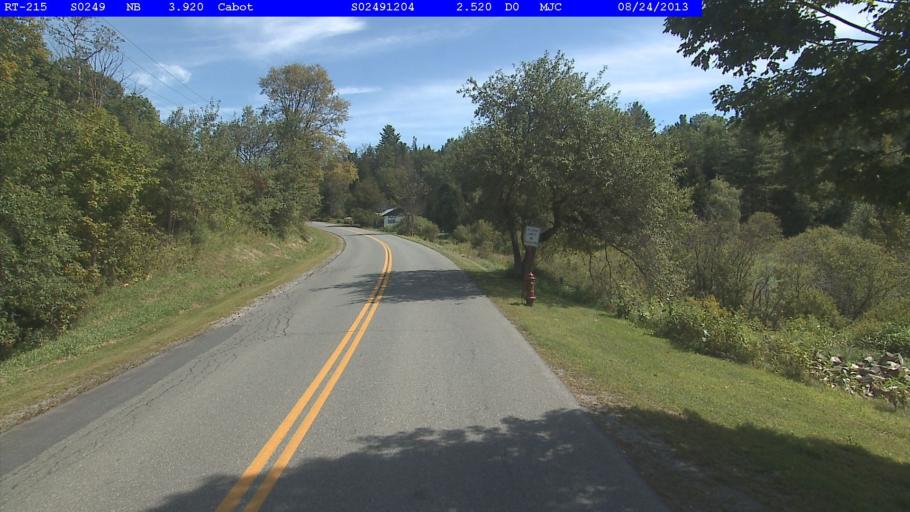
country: US
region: Vermont
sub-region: Caledonia County
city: Hardwick
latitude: 44.3985
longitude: -72.3211
